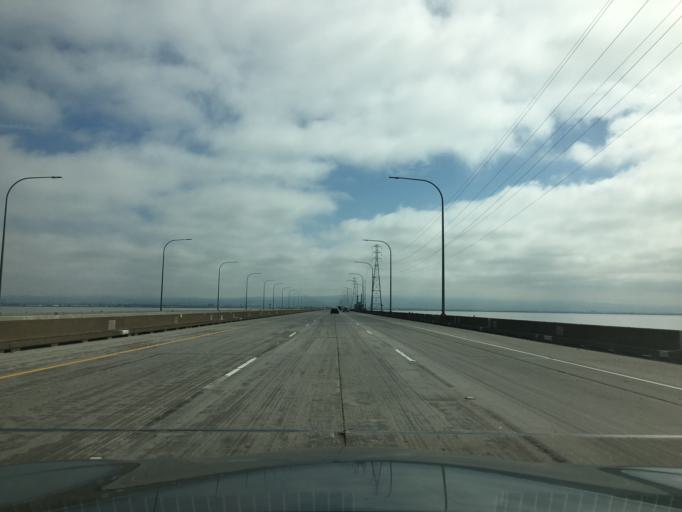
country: US
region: California
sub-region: Alameda County
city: San Lorenzo
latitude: 37.6074
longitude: -122.1872
